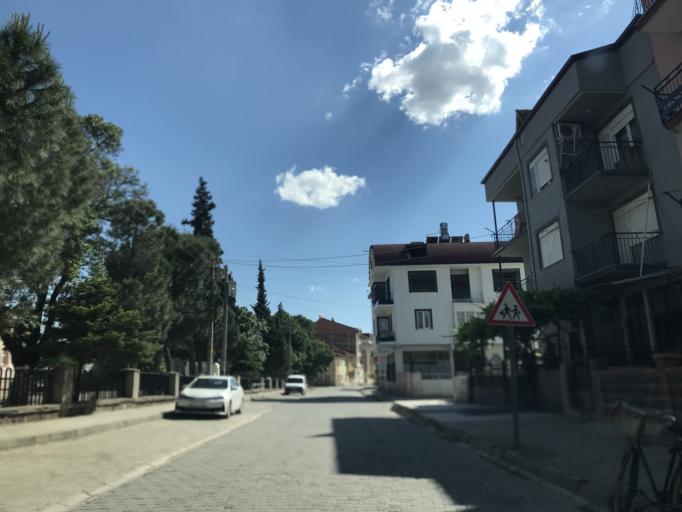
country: TR
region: Denizli
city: Civril
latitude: 38.3012
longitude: 29.7430
